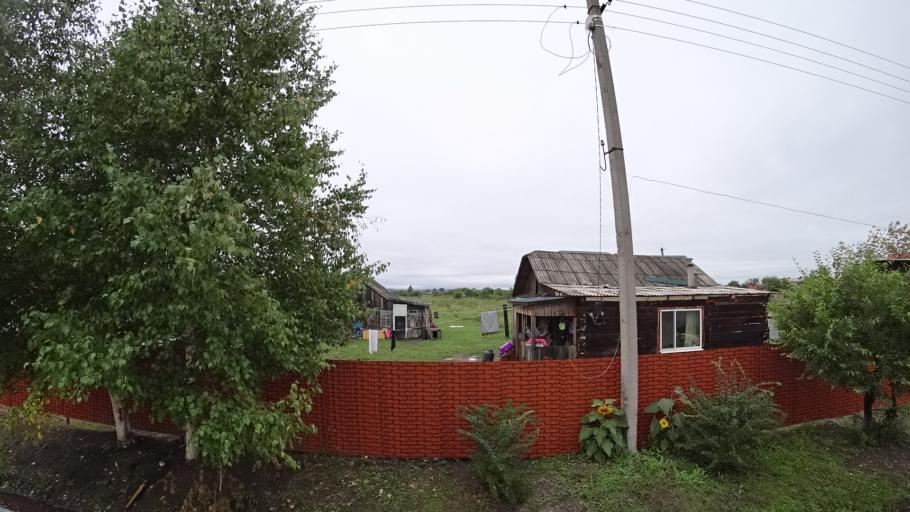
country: RU
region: Primorskiy
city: Monastyrishche
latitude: 44.1975
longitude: 132.4975
